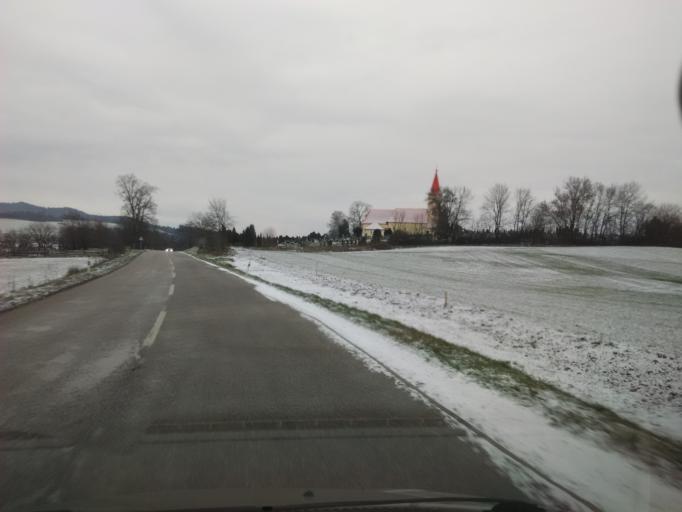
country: SK
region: Nitriansky
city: Partizanske
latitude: 48.6178
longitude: 18.4311
